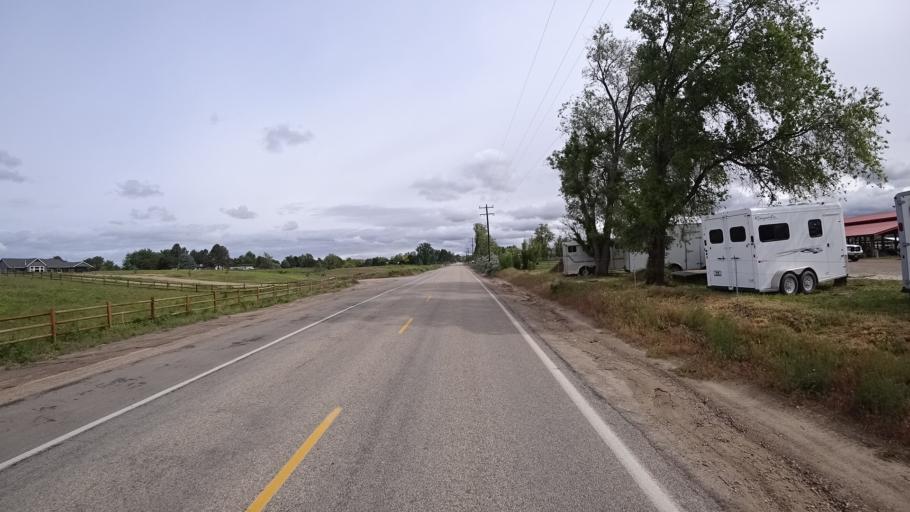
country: US
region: Idaho
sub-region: Ada County
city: Eagle
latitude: 43.7231
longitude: -116.3542
